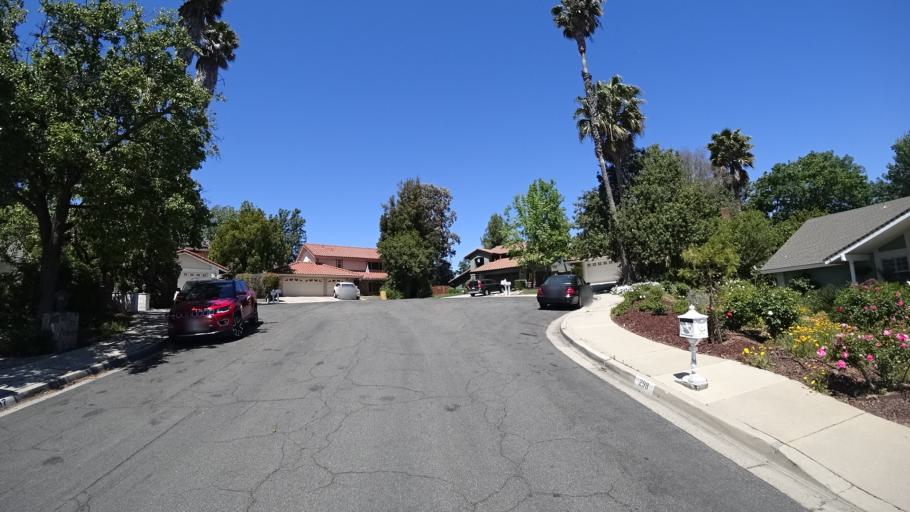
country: US
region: California
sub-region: Ventura County
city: Casa Conejo
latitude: 34.1821
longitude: -118.9007
